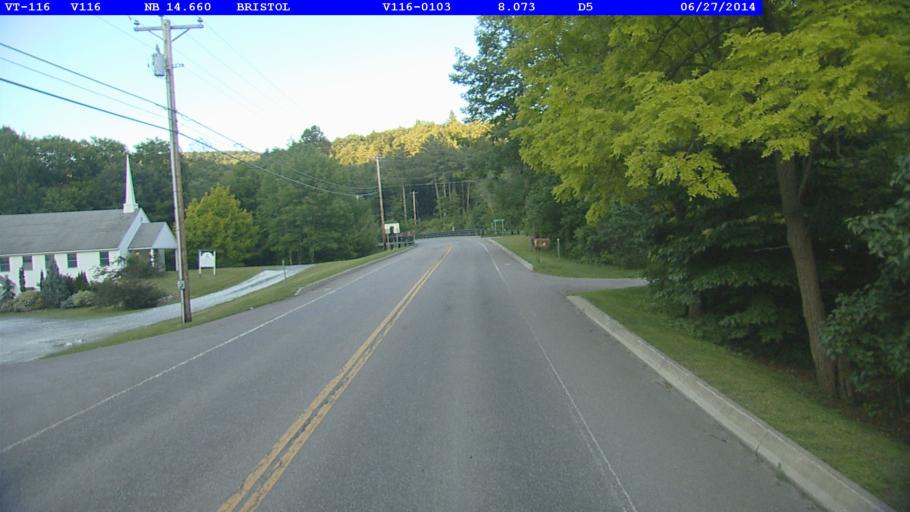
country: US
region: Vermont
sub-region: Addison County
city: Bristol
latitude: 44.1290
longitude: -73.0518
